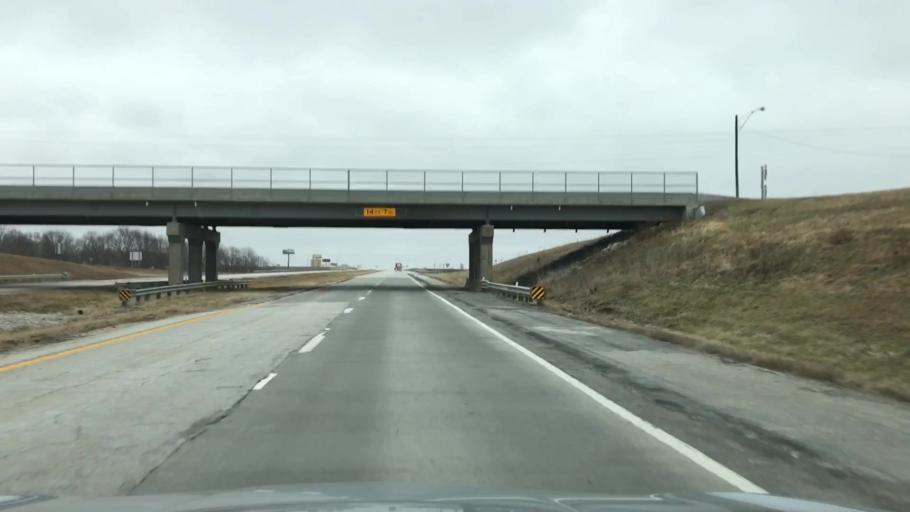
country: US
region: Missouri
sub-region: Caldwell County
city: Hamilton
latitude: 39.7334
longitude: -94.0011
